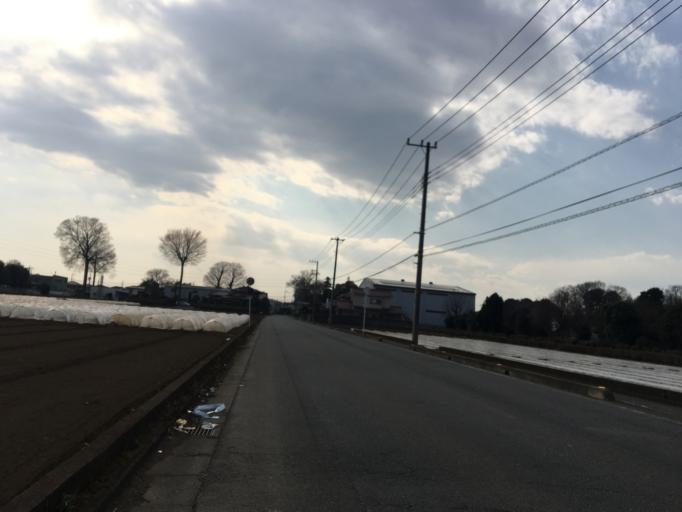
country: JP
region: Saitama
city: Oi
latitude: 35.8231
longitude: 139.5139
